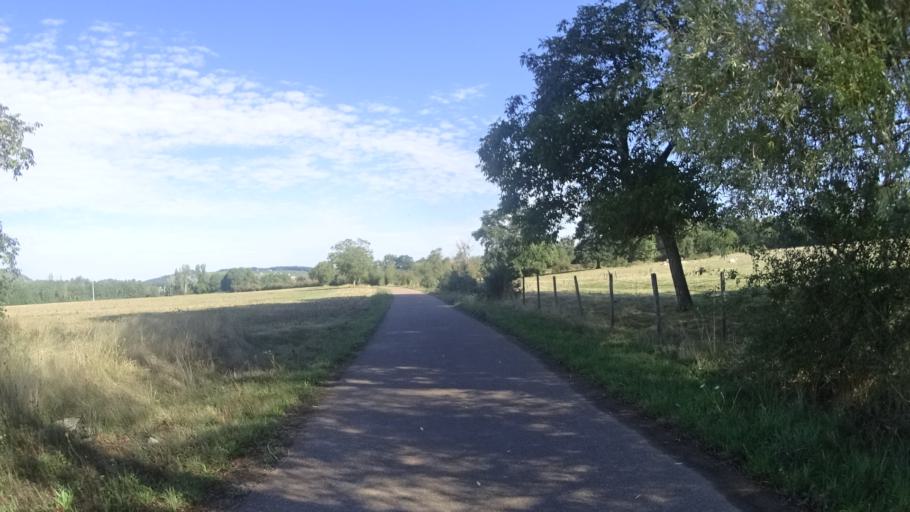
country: FR
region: Centre
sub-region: Departement du Cher
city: Sancerre
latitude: 47.3231
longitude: 2.8671
